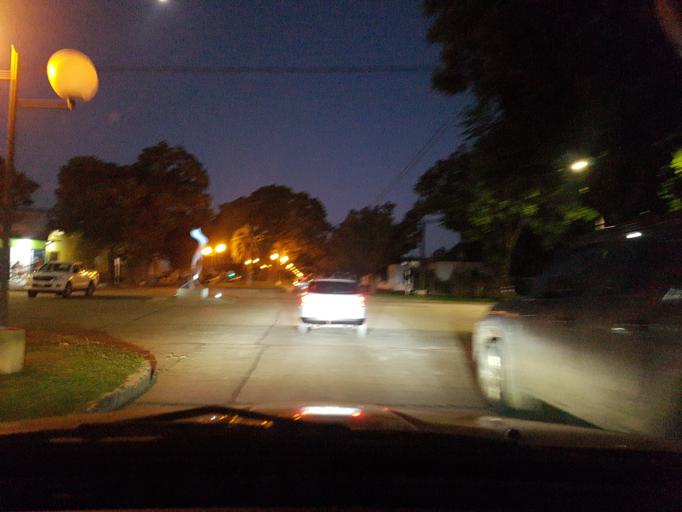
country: AR
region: Cordoba
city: Las Perdices
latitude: -32.7593
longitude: -63.7859
